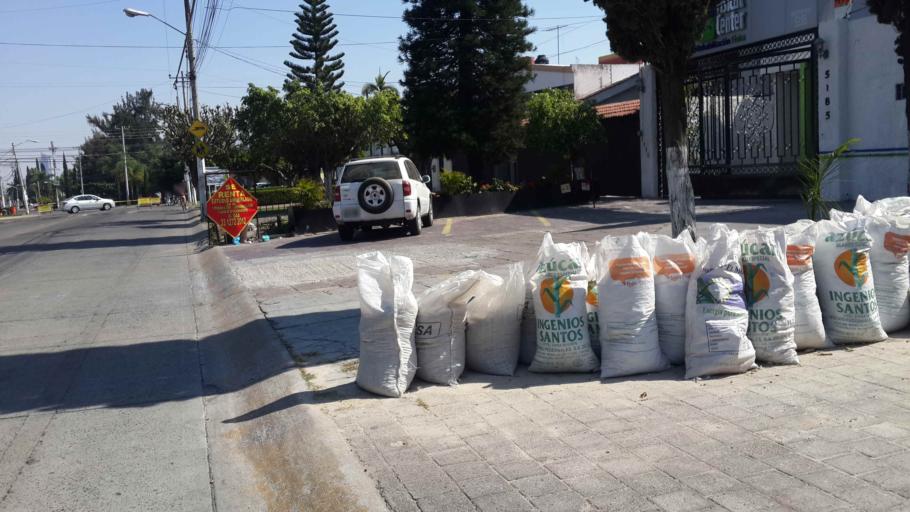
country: MX
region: Jalisco
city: Guadalajara
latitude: 20.6691
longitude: -103.4285
